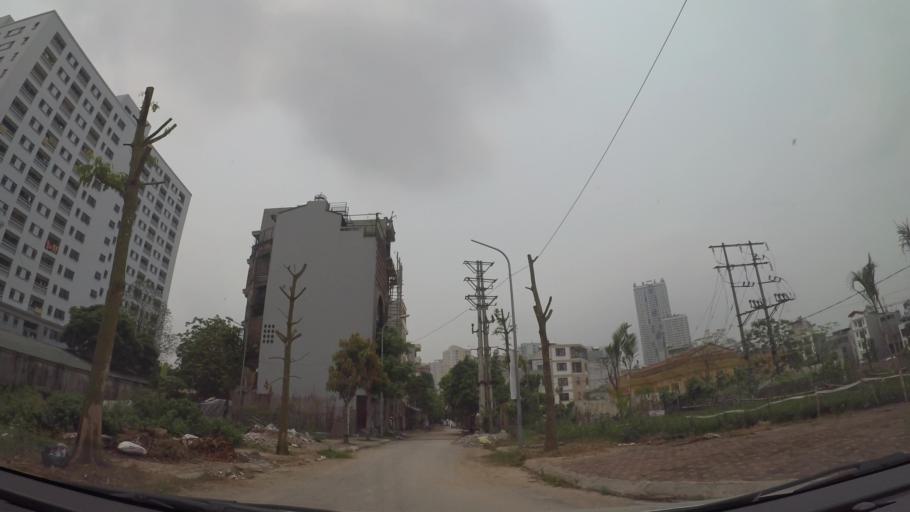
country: VN
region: Ha Noi
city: Ha Dong
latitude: 20.9754
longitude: 105.7684
